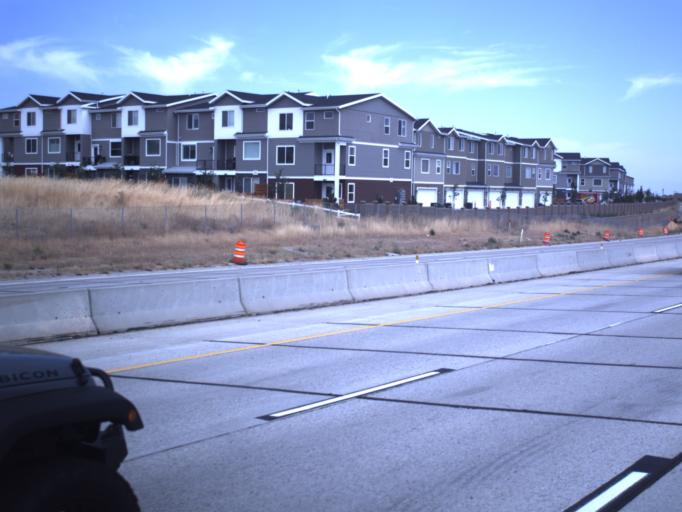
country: US
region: Utah
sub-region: Salt Lake County
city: South Jordan Heights
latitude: 40.5532
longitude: -111.9779
